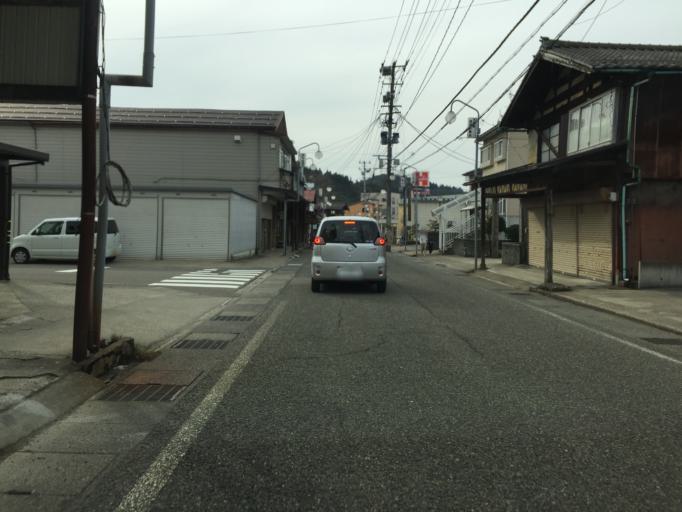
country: JP
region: Niigata
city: Tochio-honcho
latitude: 37.4726
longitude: 138.9987
